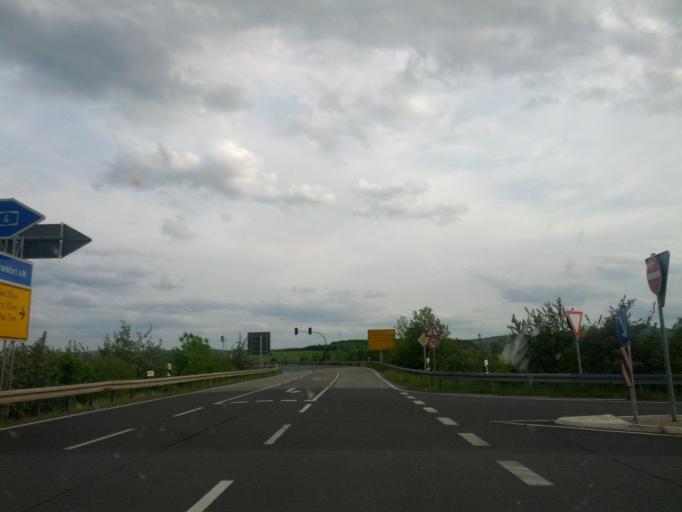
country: DE
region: Thuringia
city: Horselgau
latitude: 50.9055
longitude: 10.6113
